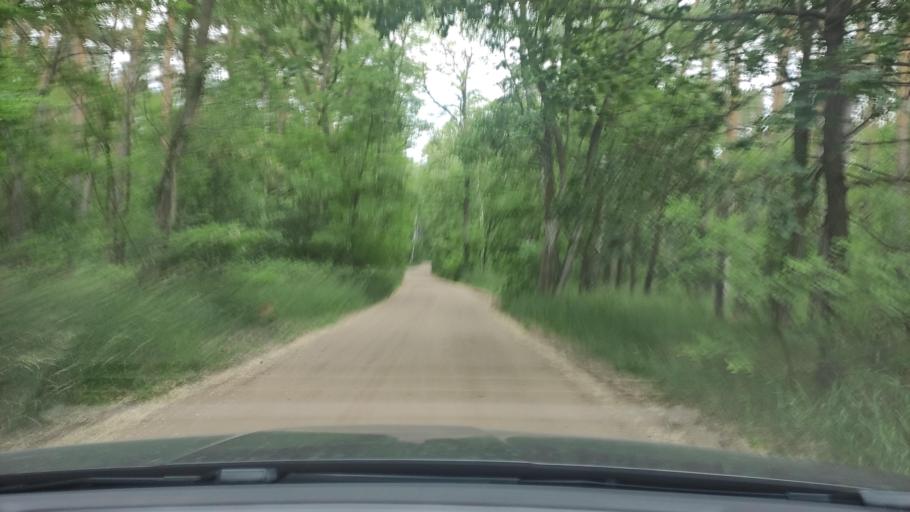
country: PL
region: Greater Poland Voivodeship
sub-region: Powiat poznanski
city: Pobiedziska
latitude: 52.4989
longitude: 17.2026
